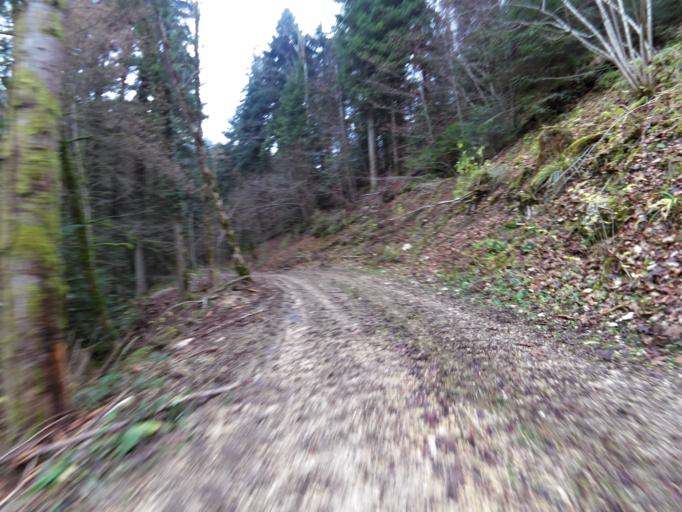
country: FR
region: Alsace
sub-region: Departement du Haut-Rhin
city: Ferrette
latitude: 47.4339
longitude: 7.2813
